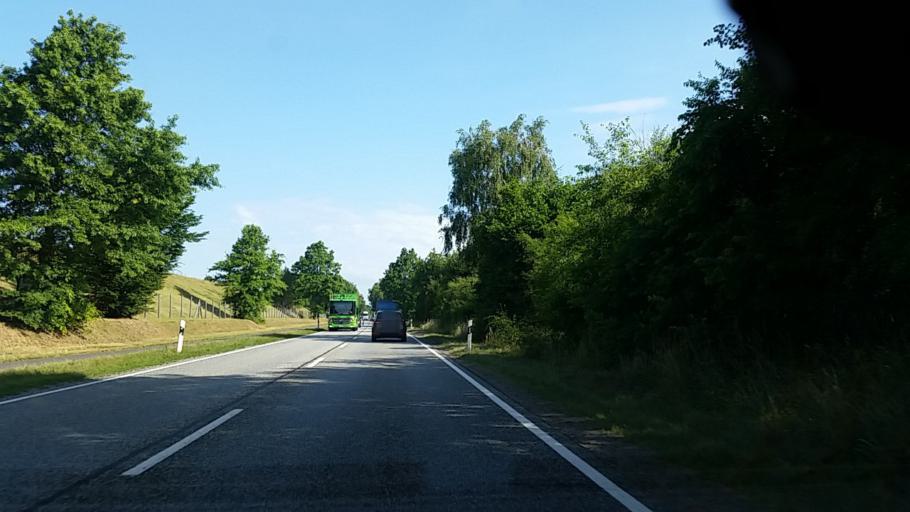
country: DE
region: Hamburg
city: Langenhorn
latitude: 53.7148
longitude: 10.0295
